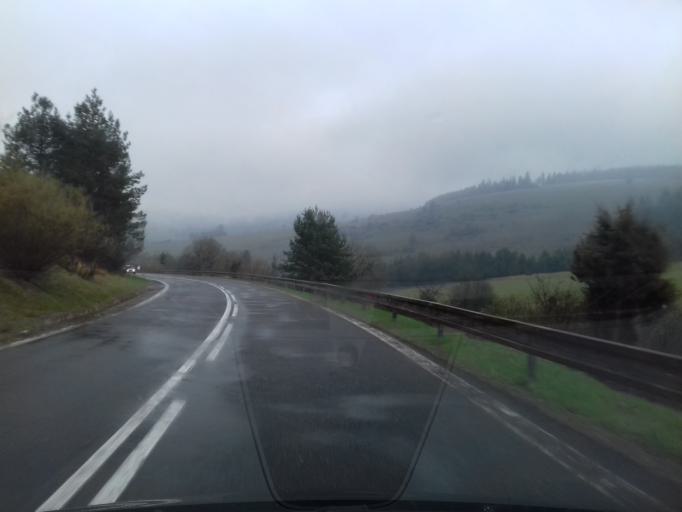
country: SK
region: Presovsky
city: Stara L'ubovna
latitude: 49.3575
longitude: 20.6862
